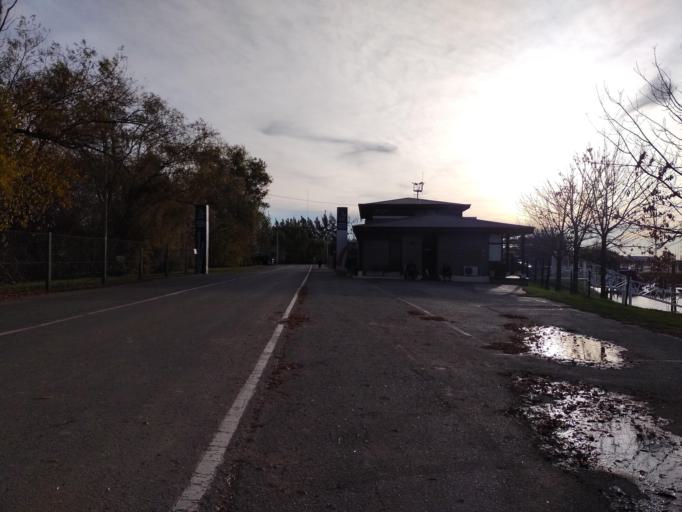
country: AR
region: Buenos Aires
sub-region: Partido de San Isidro
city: San Isidro
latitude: -34.4443
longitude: -58.5322
